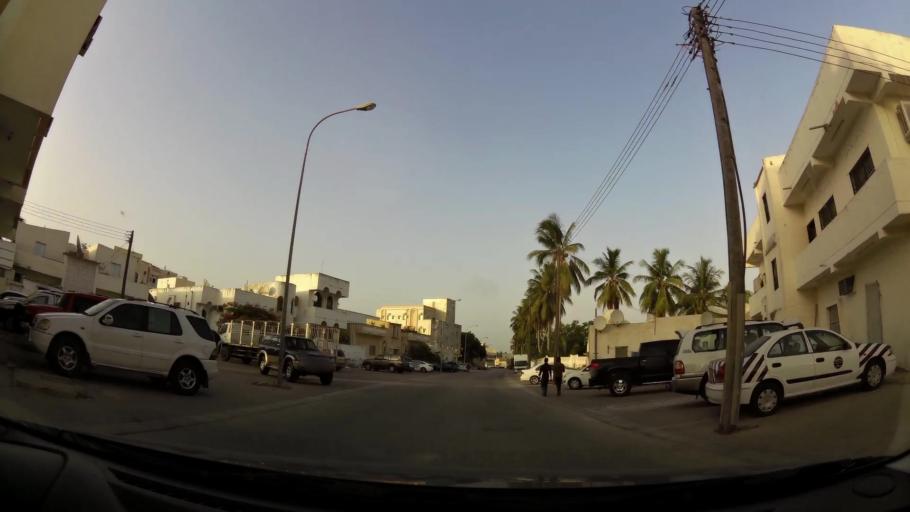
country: OM
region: Zufar
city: Salalah
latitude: 17.0145
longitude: 54.1115
